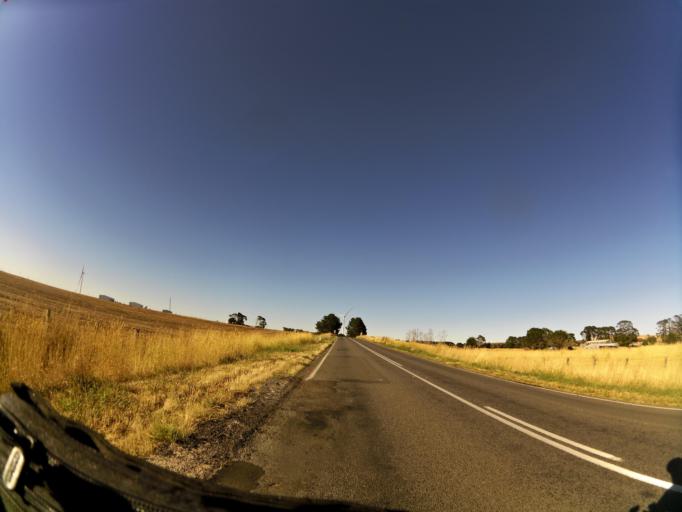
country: AU
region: Victoria
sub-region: Ballarat North
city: Delacombe
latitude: -37.5583
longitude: 143.3641
